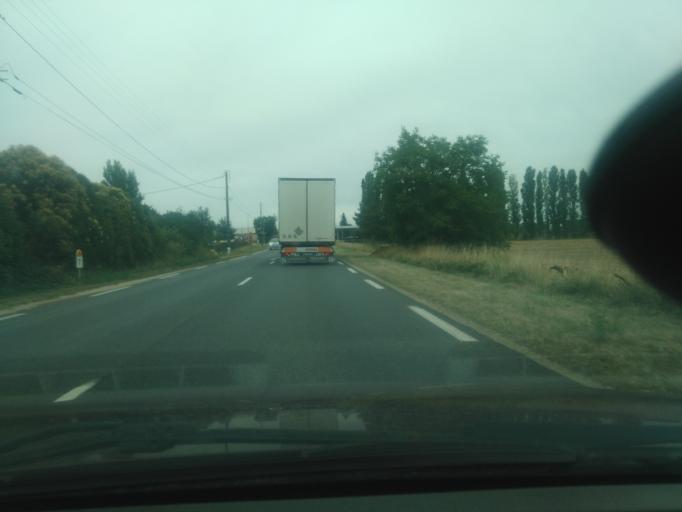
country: FR
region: Poitou-Charentes
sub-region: Departement de la Vienne
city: Sevres-Anxaumont
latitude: 46.5594
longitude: 0.4559
